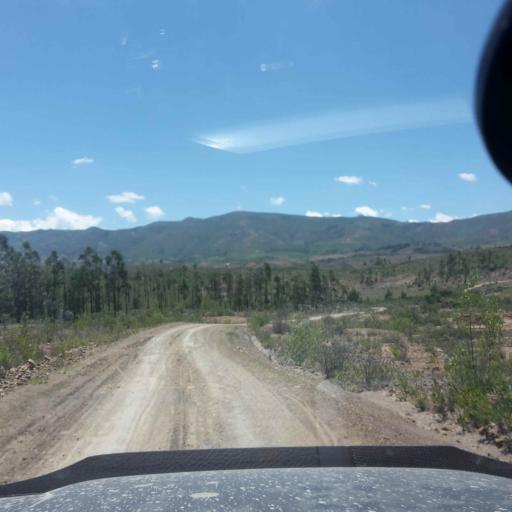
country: BO
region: Cochabamba
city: Totora
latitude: -17.7716
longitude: -65.2651
